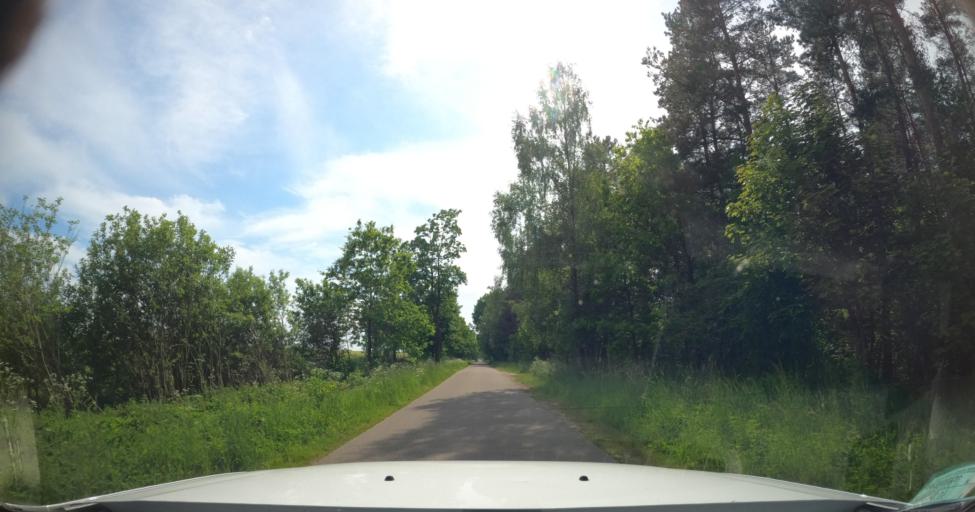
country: PL
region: Warmian-Masurian Voivodeship
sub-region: Powiat lidzbarski
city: Lubomino
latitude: 54.0978
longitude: 20.3156
